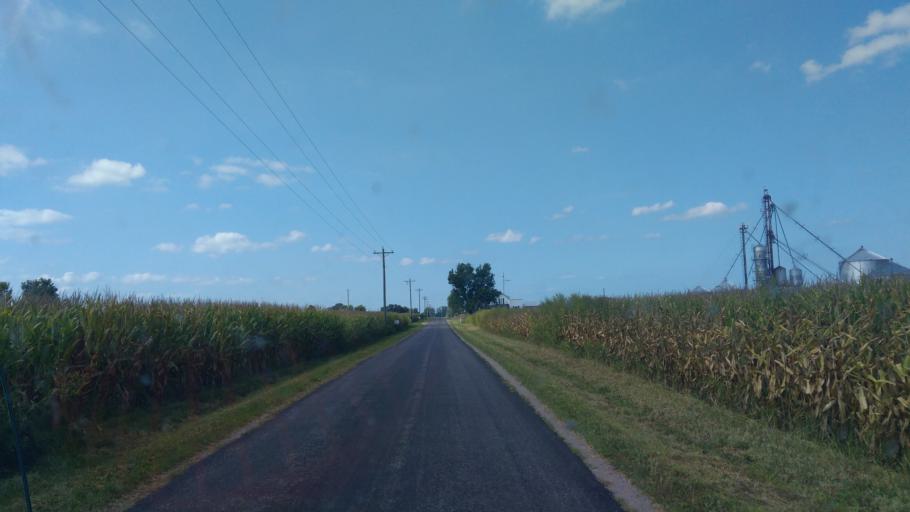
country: US
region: Ohio
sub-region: Union County
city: Richwood
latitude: 40.4577
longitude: -83.3955
